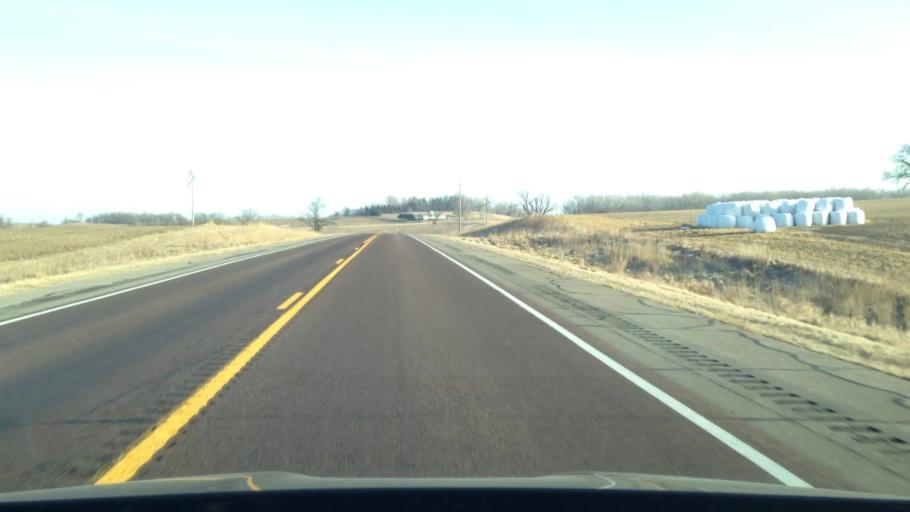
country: US
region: Minnesota
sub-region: Goodhue County
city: Goodhue
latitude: 44.4352
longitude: -92.6140
